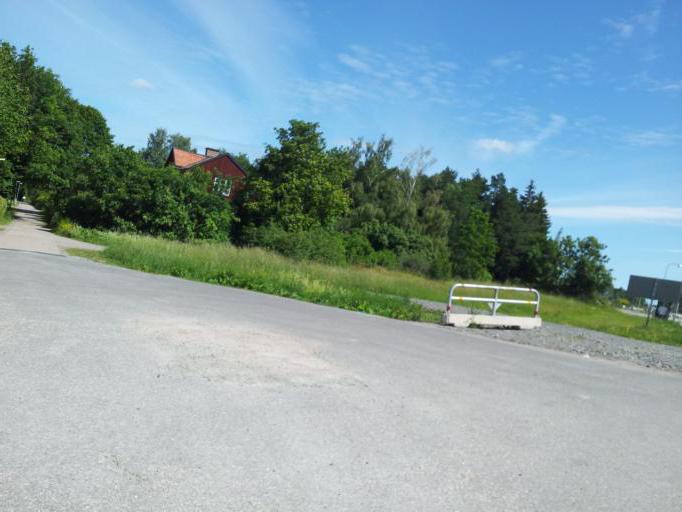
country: SE
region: Uppsala
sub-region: Uppsala Kommun
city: Uppsala
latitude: 59.8736
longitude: 17.6712
